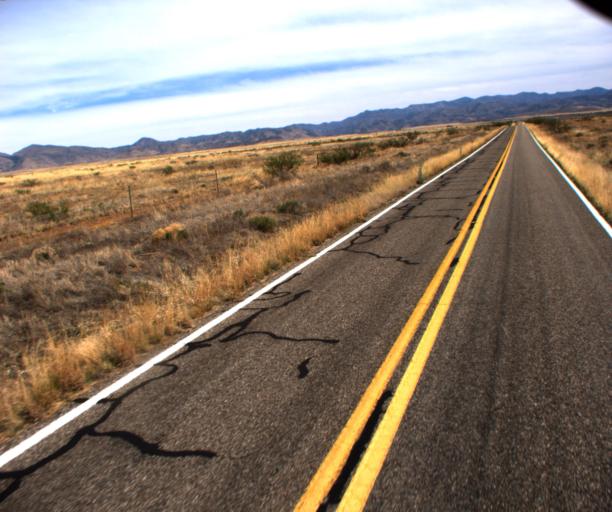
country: US
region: Arizona
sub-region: Cochise County
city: Willcox
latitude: 32.0552
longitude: -109.4962
